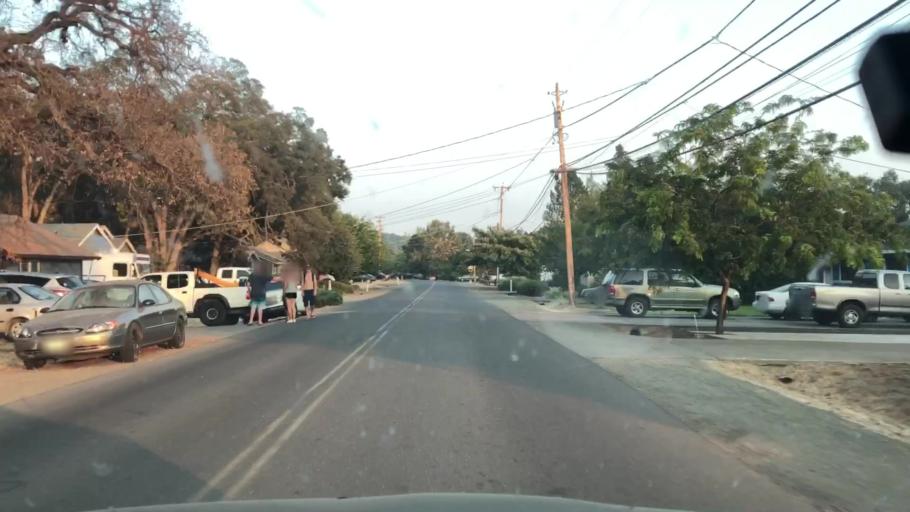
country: US
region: California
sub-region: Lake County
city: Hidden Valley Lake
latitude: 38.7944
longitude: -122.5518
